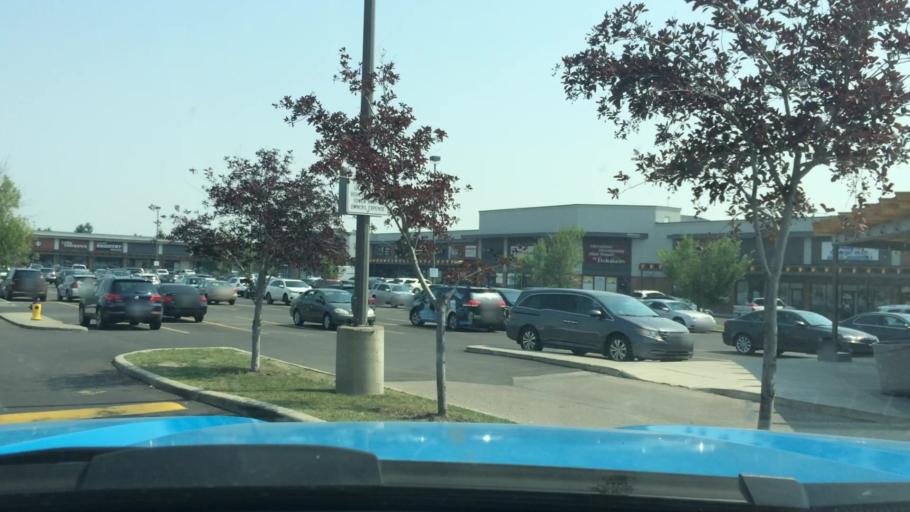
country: CA
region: Alberta
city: Calgary
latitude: 51.1380
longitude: -114.1598
